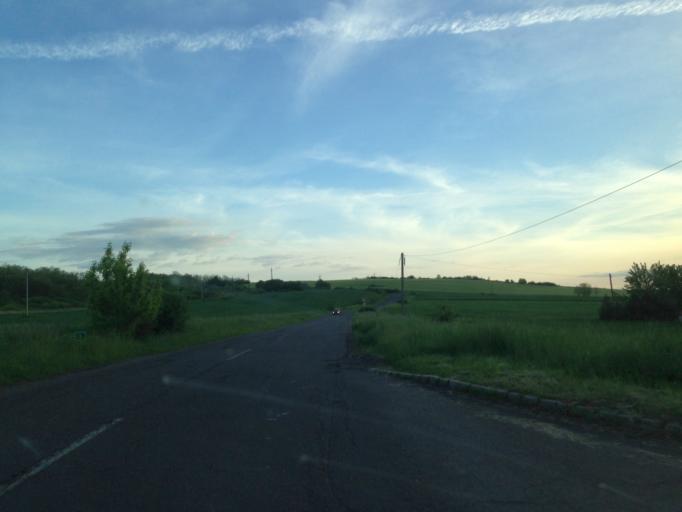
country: HU
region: Nograd
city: Tar
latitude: 47.9442
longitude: 19.7282
